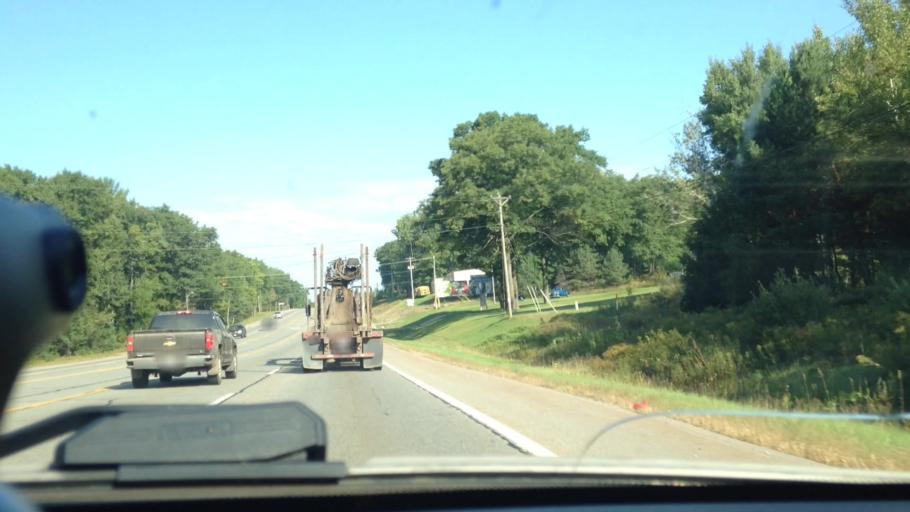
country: US
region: Michigan
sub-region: Dickinson County
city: Iron Mountain
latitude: 45.8537
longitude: -88.0554
